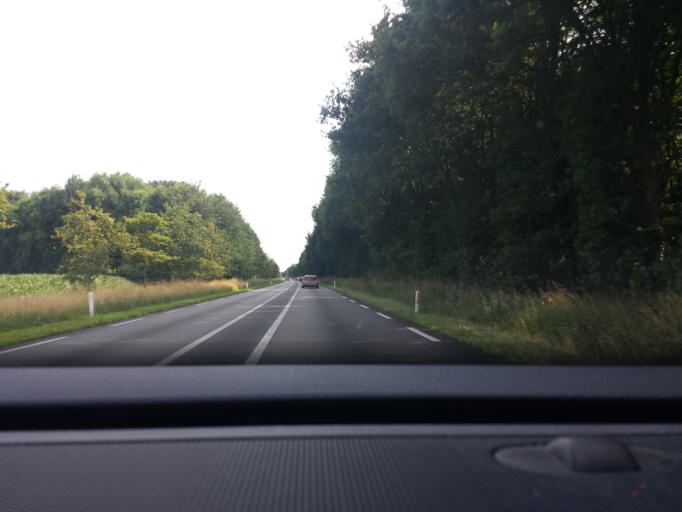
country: NL
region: Gelderland
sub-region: Gemeente Lochem
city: Laren
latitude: 52.1924
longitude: 6.3712
